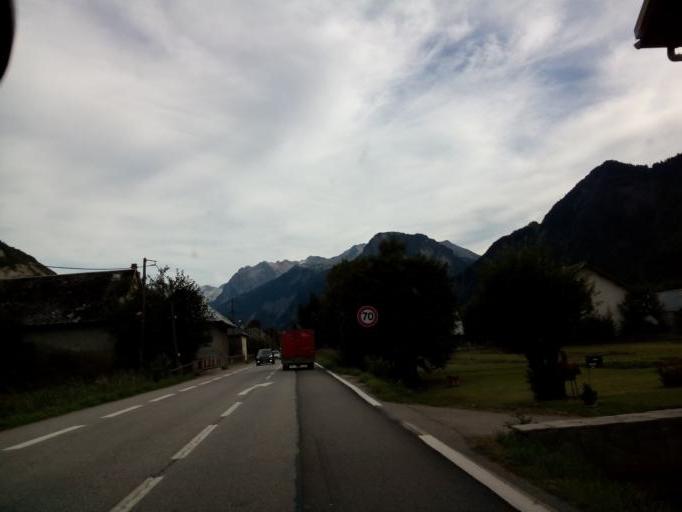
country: FR
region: Rhone-Alpes
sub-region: Departement de l'Isere
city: Huez
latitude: 45.1001
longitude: 6.0091
